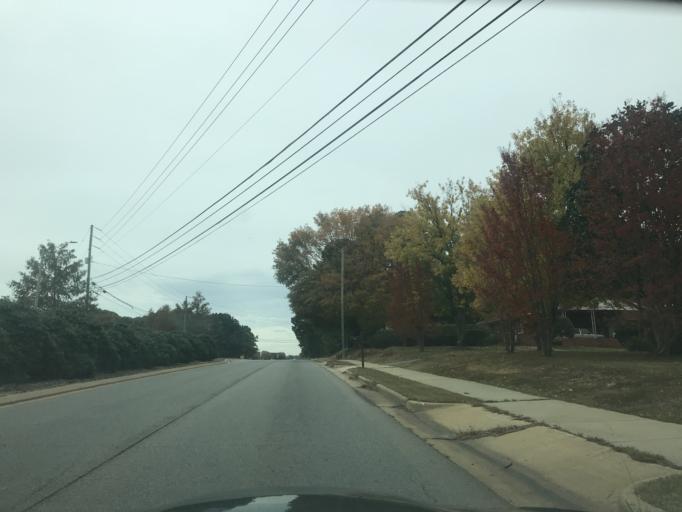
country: US
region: North Carolina
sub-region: Wake County
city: West Raleigh
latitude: 35.8682
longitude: -78.6801
